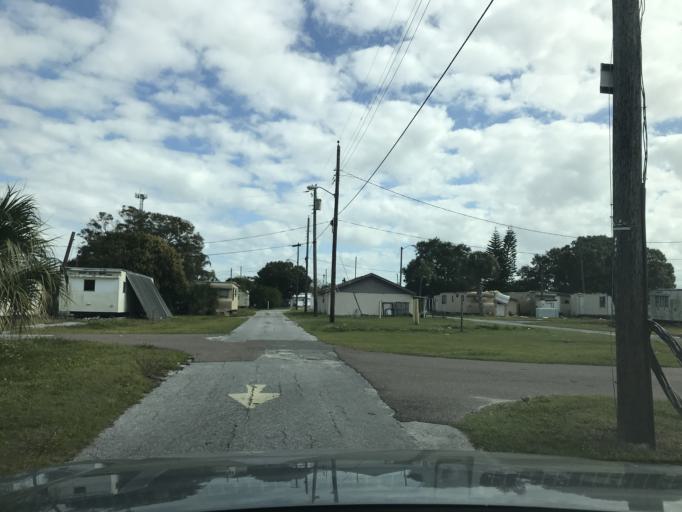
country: US
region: Florida
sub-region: Pinellas County
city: Belleair
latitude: 27.9382
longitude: -82.7987
